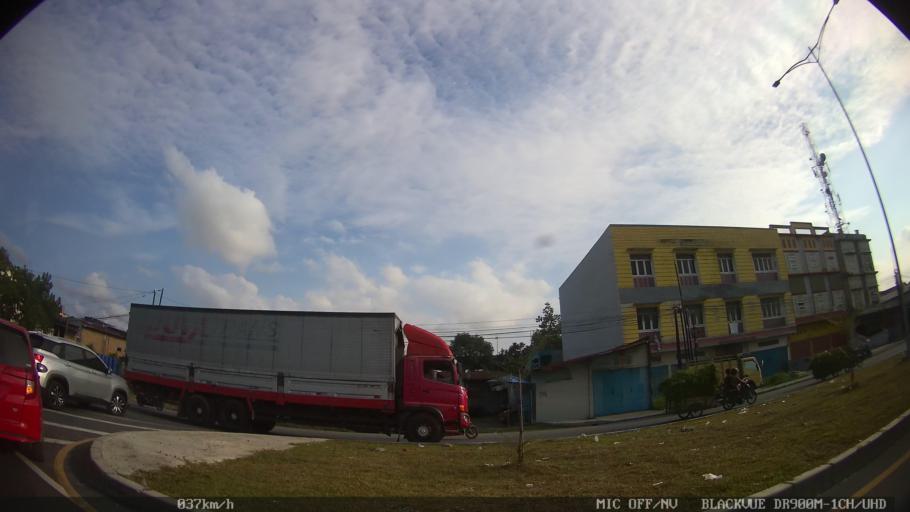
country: ID
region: North Sumatra
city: Medan
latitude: 3.6156
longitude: 98.6436
